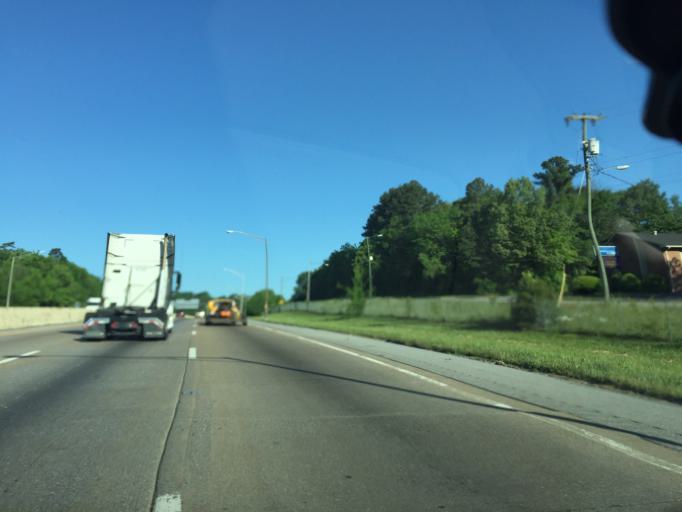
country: US
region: Tennessee
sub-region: Hamilton County
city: East Ridge
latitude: 35.0127
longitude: -85.2478
